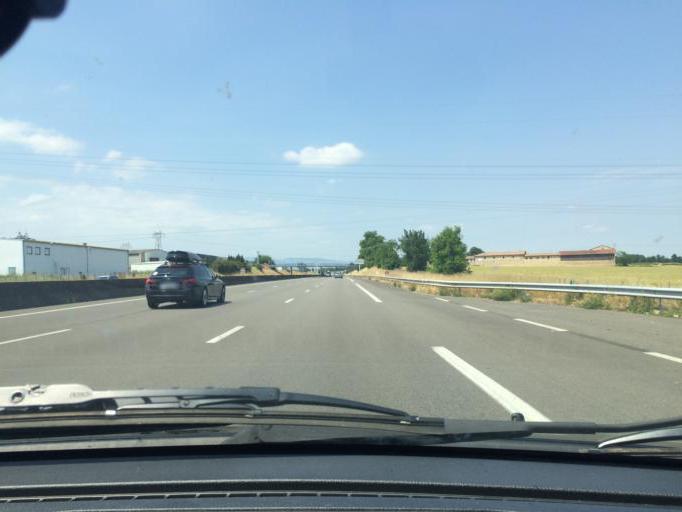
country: FR
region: Rhone-Alpes
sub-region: Departement du Rhone
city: Arnas
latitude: 46.0091
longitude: 4.7309
